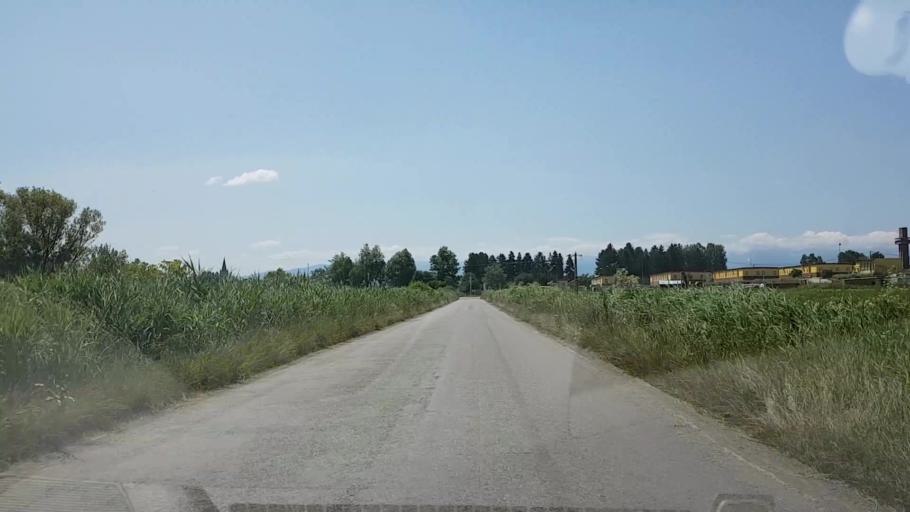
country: RO
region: Brasov
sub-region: Comuna Cincu
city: Cincu
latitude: 45.9275
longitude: 24.7959
